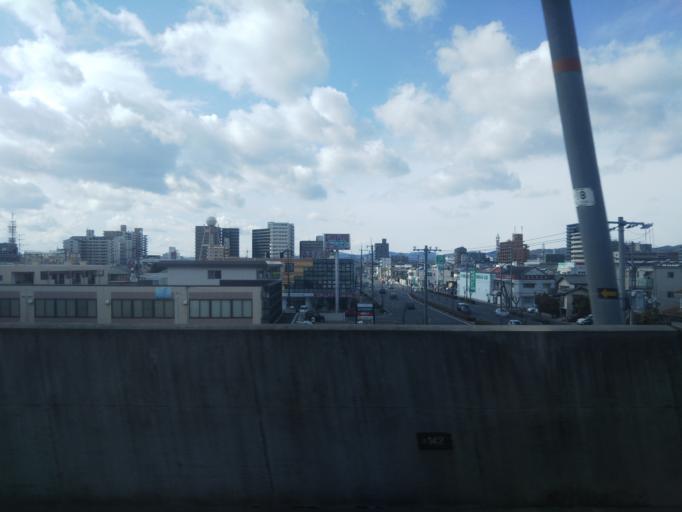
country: JP
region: Okayama
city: Okayama-shi
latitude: 34.6431
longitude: 133.9108
